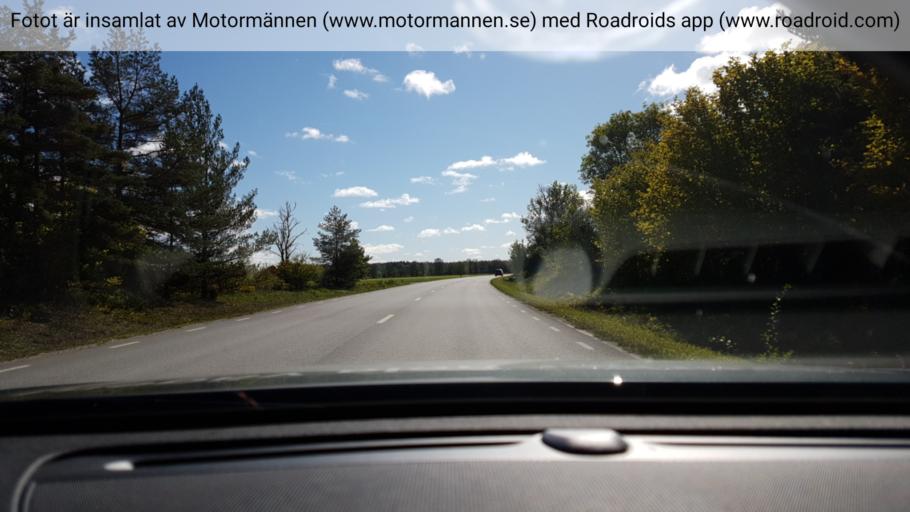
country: SE
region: Gotland
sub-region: Gotland
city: Slite
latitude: 57.7693
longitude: 18.7867
